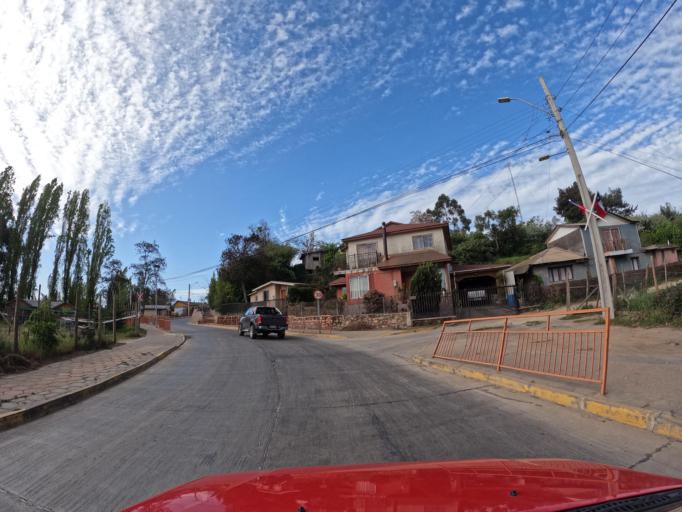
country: CL
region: Valparaiso
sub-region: San Antonio Province
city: San Antonio
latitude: -34.1189
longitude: -71.7271
